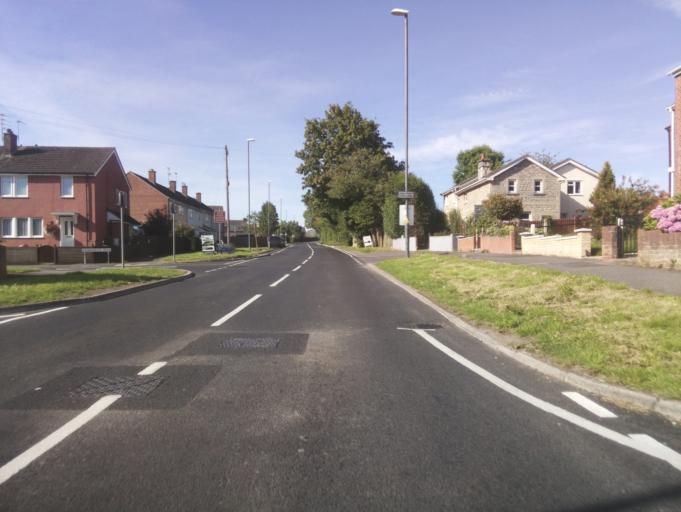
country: GB
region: England
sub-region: Bath and North East Somerset
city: Keynsham
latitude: 51.4081
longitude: -2.5144
